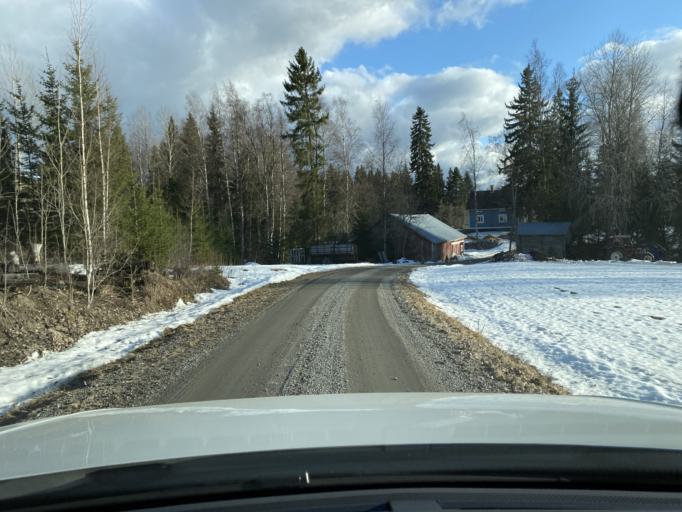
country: FI
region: Pirkanmaa
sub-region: Lounais-Pirkanmaa
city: Mouhijaervi
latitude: 61.4604
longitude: 22.9591
